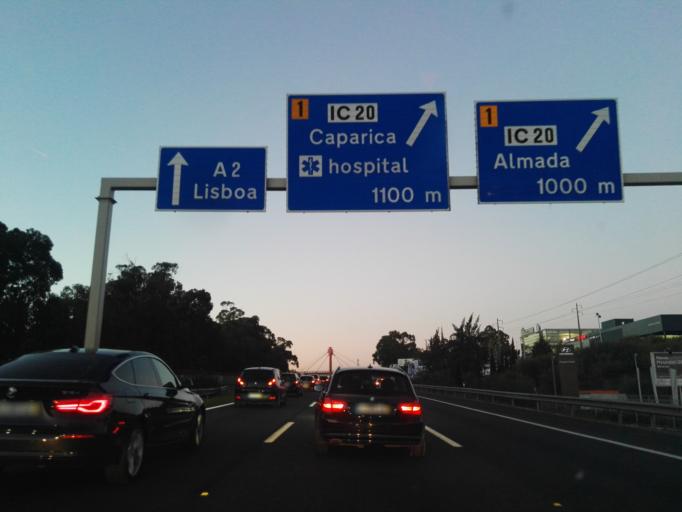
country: PT
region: Setubal
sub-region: Almada
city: Sobreda
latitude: 38.6532
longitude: -9.1689
